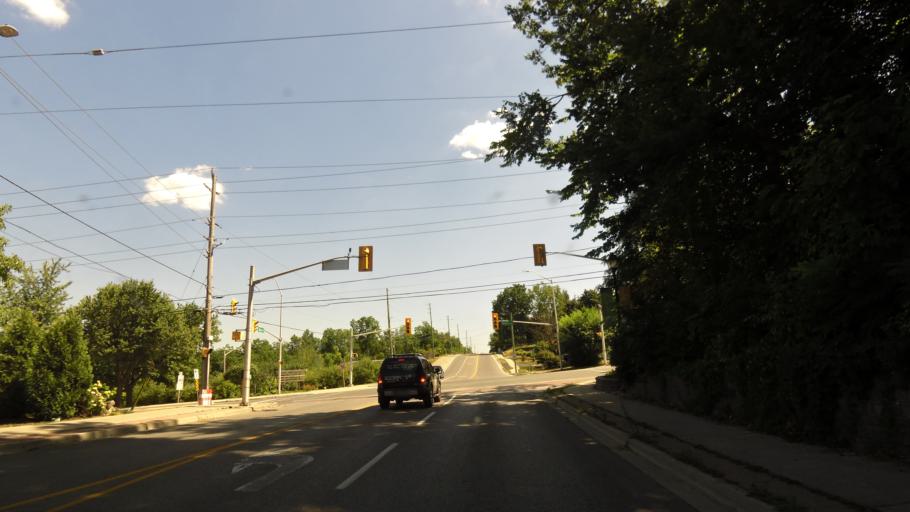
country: CA
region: Ontario
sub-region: Halton
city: Milton
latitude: 43.6460
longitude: -79.9216
